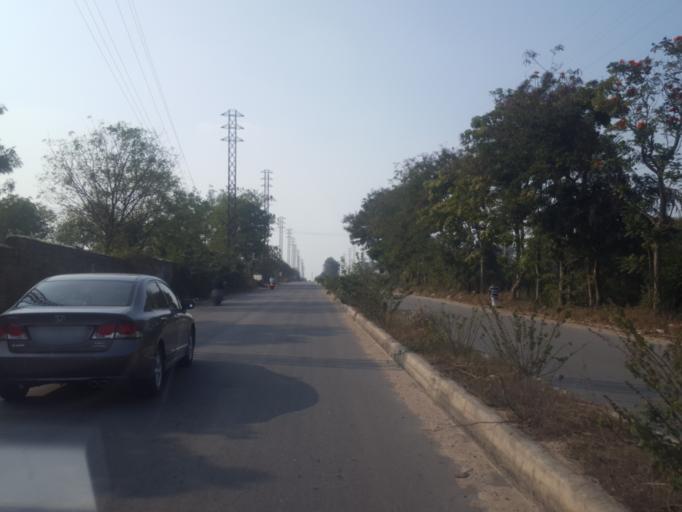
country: IN
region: Telangana
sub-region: Medak
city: Serilingampalle
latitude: 17.4138
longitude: 78.2642
